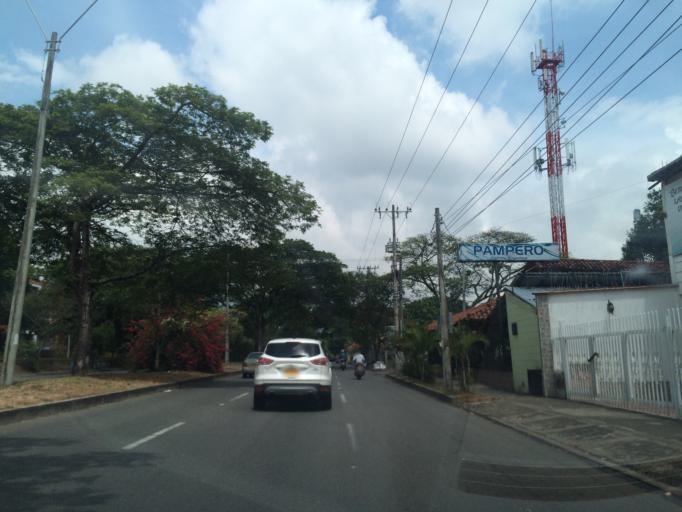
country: CO
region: Valle del Cauca
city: Cali
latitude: 3.3933
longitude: -76.5348
